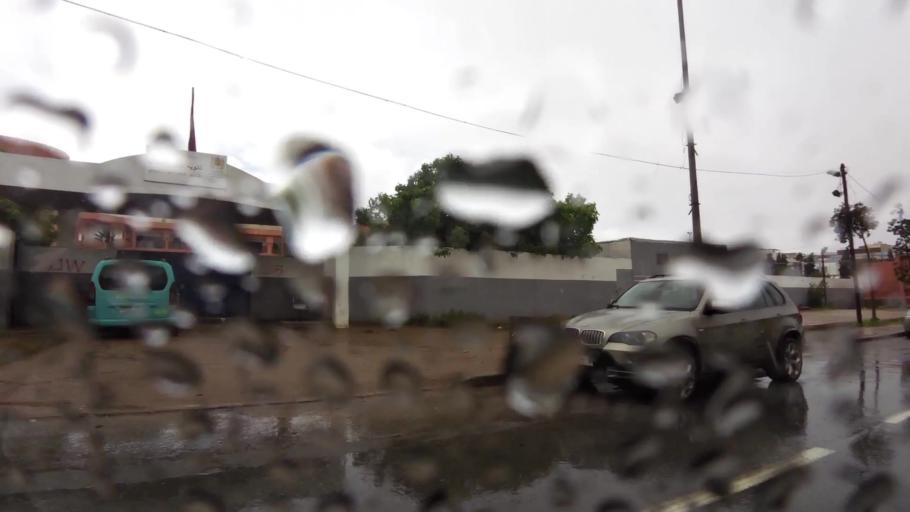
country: MA
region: Grand Casablanca
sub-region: Casablanca
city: Casablanca
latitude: 33.5490
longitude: -7.6792
